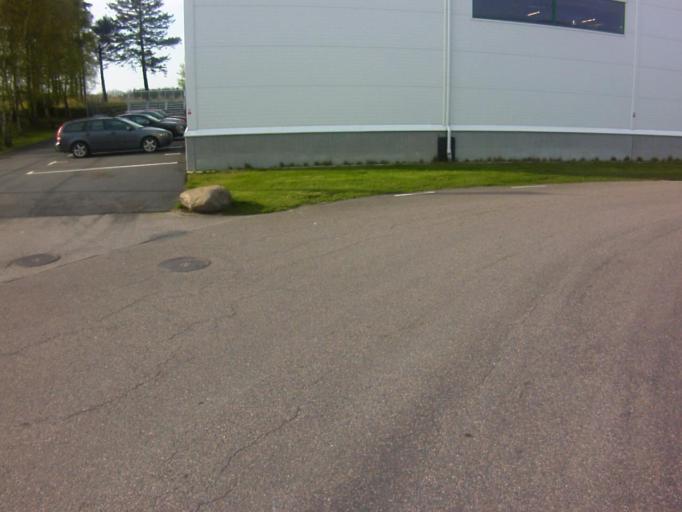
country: SE
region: Skane
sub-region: Kavlinge Kommun
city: Loddekopinge
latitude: 55.7705
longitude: 12.9998
